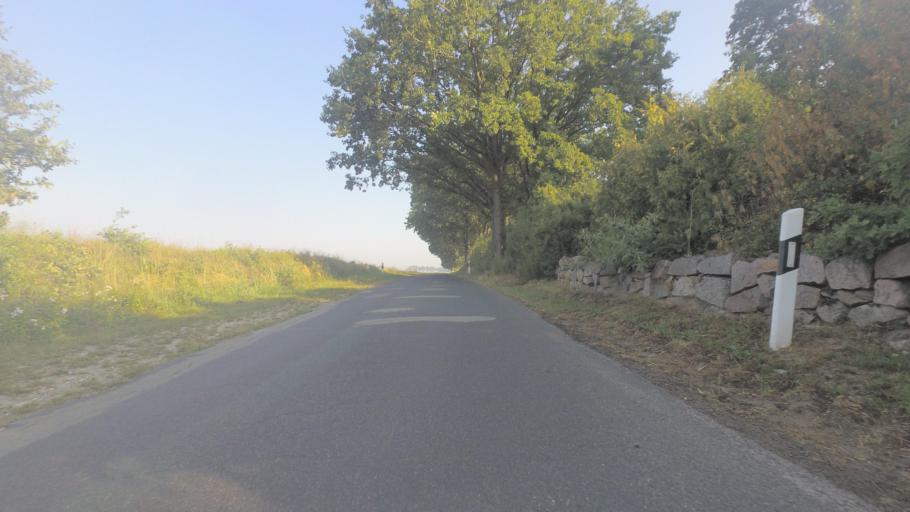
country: DE
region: Brandenburg
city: Heiligengrabe
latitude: 53.2491
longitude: 12.3485
